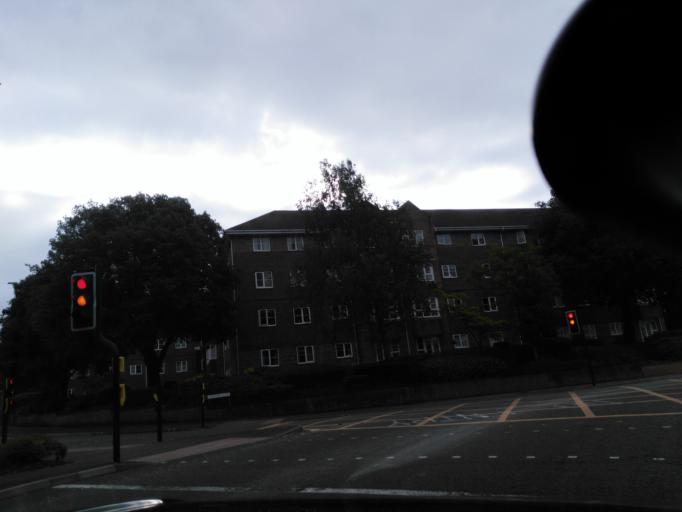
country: GB
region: England
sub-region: Dorset
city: Parkstone
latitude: 50.7232
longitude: -1.9597
